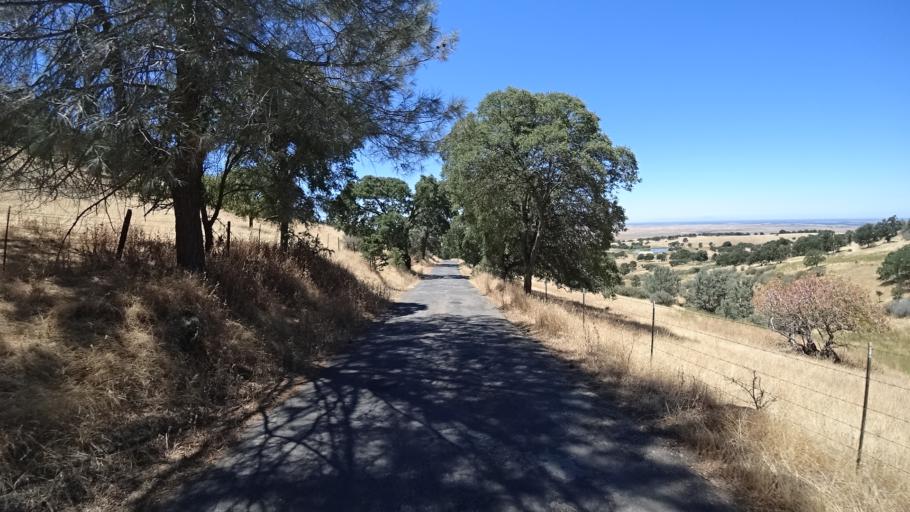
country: US
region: California
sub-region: Calaveras County
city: Rancho Calaveras
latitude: 38.0542
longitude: -120.8059
